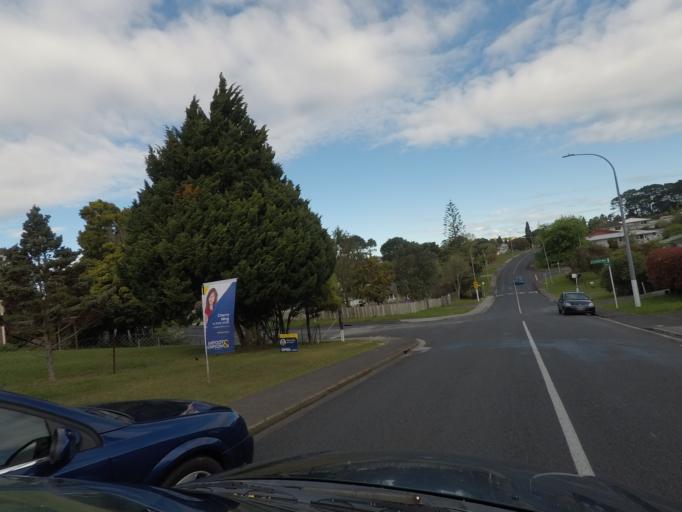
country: NZ
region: Auckland
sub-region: Auckland
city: Rosebank
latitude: -36.8868
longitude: 174.6506
